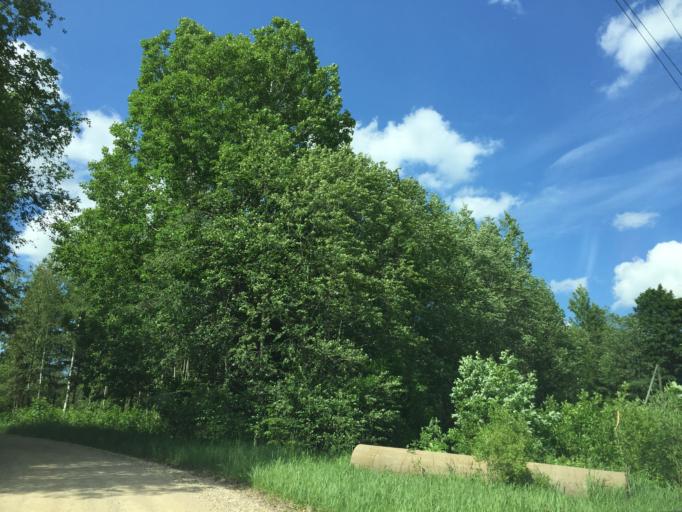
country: LV
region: Priekuli
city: Priekuli
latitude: 57.2292
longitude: 25.4361
